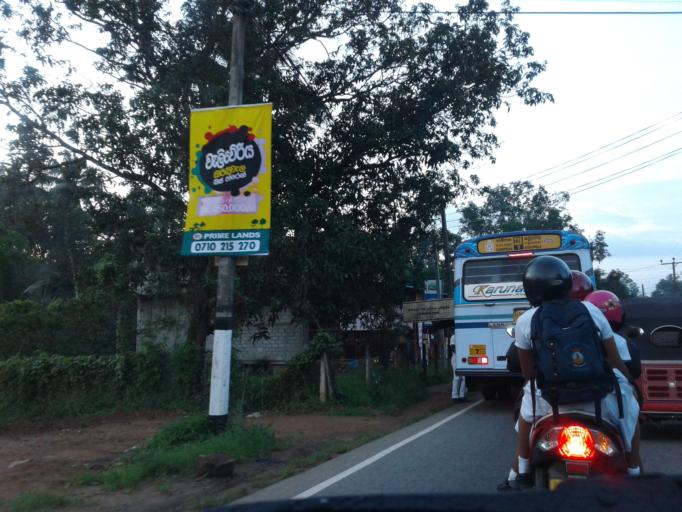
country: LK
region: Western
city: Gampaha
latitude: 7.0432
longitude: 80.0182
